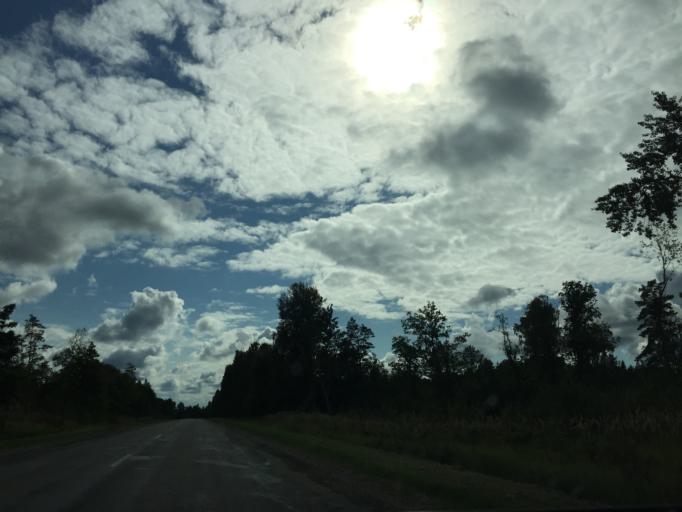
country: LV
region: Limbazu Rajons
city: Limbazi
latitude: 57.4129
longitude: 24.6962
